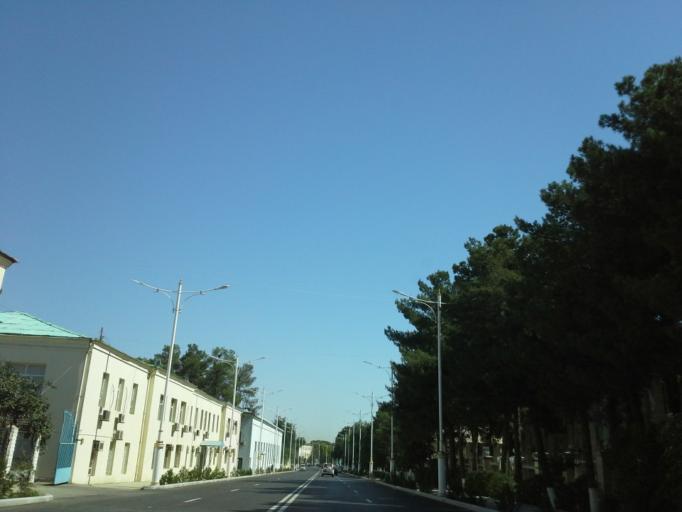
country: TM
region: Ahal
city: Ashgabat
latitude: 37.9484
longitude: 58.3542
